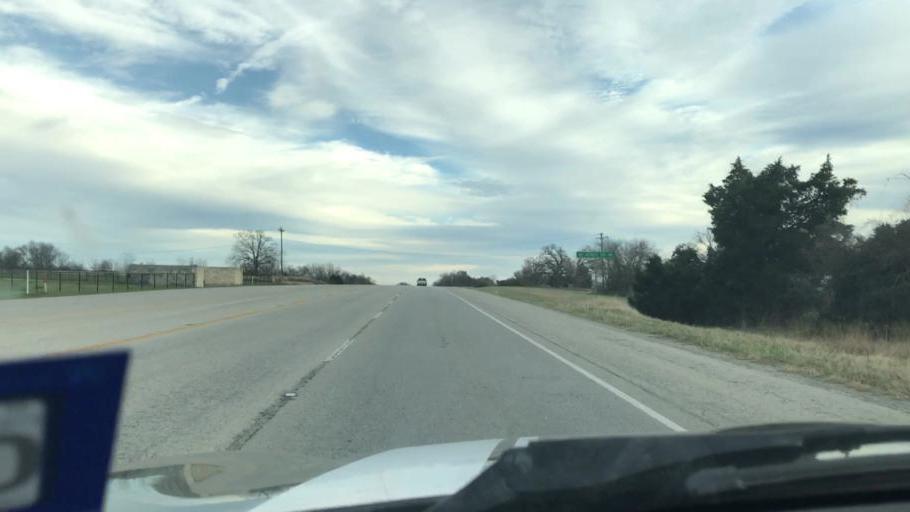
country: US
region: Texas
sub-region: Bastrop County
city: Camp Swift
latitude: 30.2896
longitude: -97.2519
